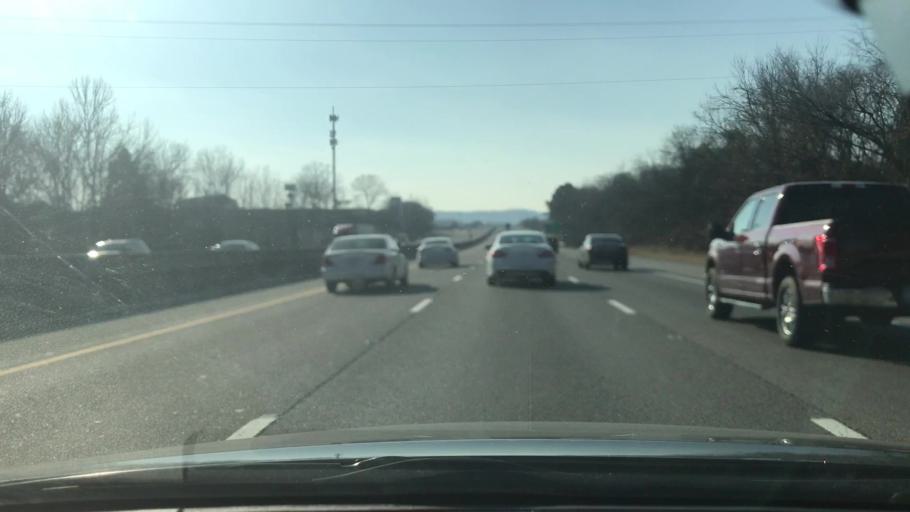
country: US
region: Tennessee
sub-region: Davidson County
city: Belle Meade
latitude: 36.0847
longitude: -86.9495
